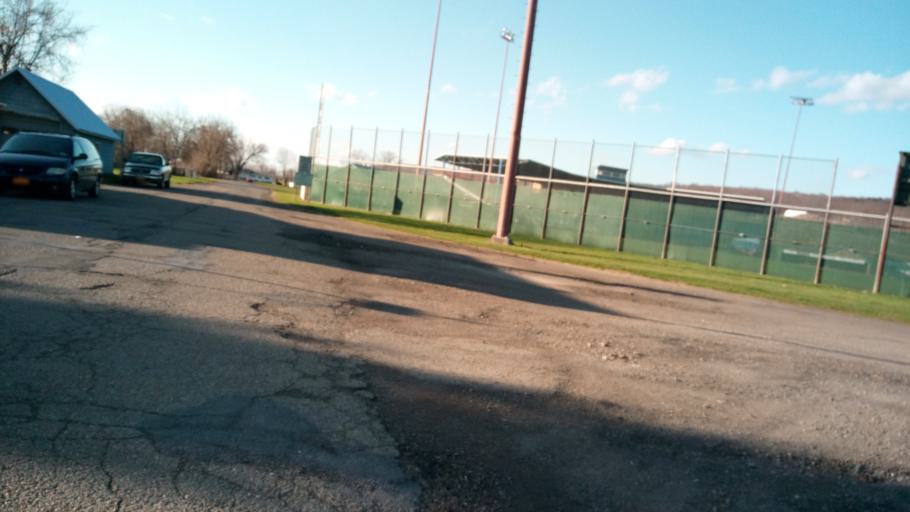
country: US
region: New York
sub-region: Chemung County
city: Elmira
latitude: 42.0790
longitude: -76.7809
